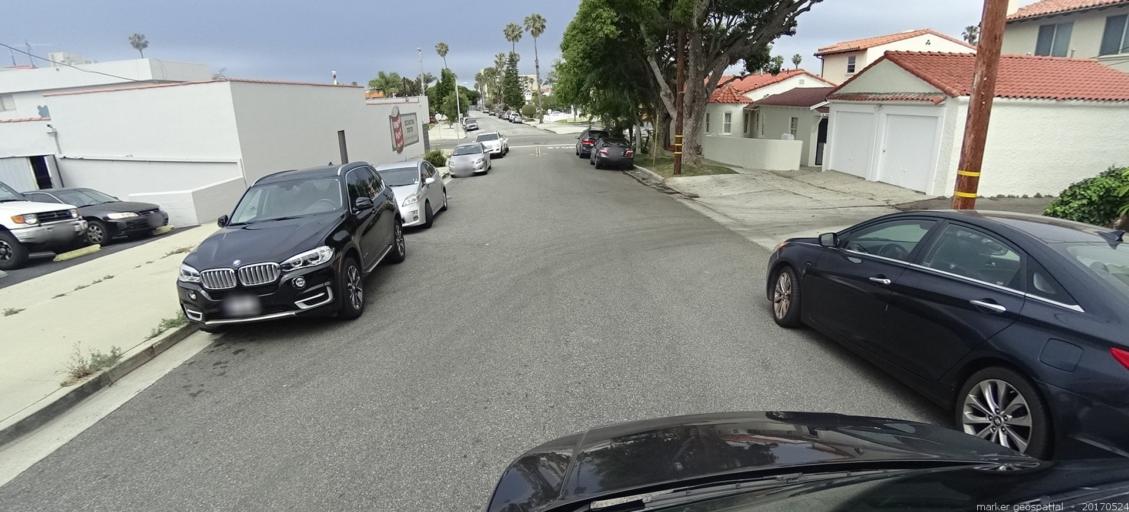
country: US
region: California
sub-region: Los Angeles County
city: Redondo Beach
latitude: 33.8267
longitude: -118.3850
